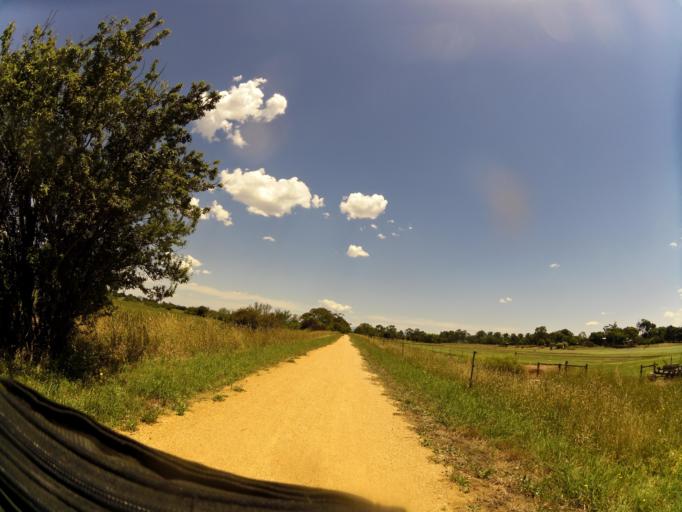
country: AU
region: Victoria
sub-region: Wellington
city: Heyfield
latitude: -37.9653
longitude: 146.8989
